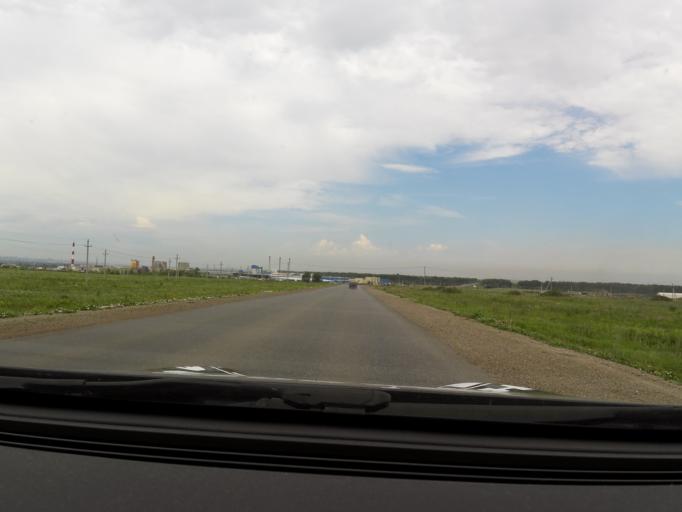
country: RU
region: Bashkortostan
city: Iglino
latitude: 54.7612
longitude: 56.2711
